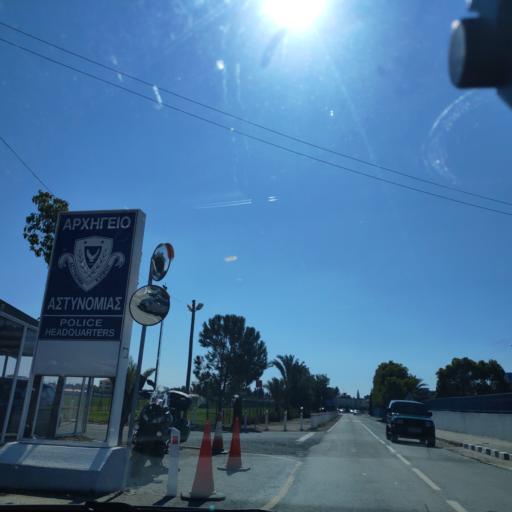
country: CY
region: Lefkosia
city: Nicosia
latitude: 35.1464
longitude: 33.3763
